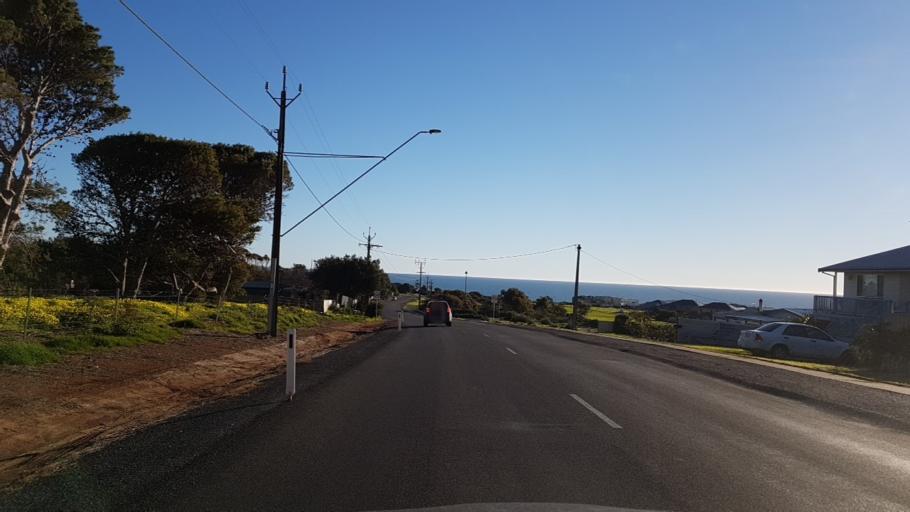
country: AU
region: South Australia
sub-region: Onkaparinga
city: Port Willunga
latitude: -35.3293
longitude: 138.4559
